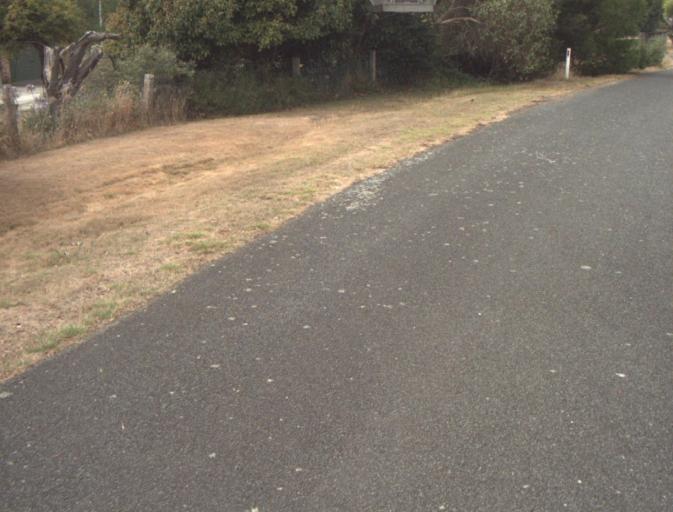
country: AU
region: Tasmania
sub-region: Launceston
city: Mayfield
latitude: -41.2794
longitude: 147.0185
